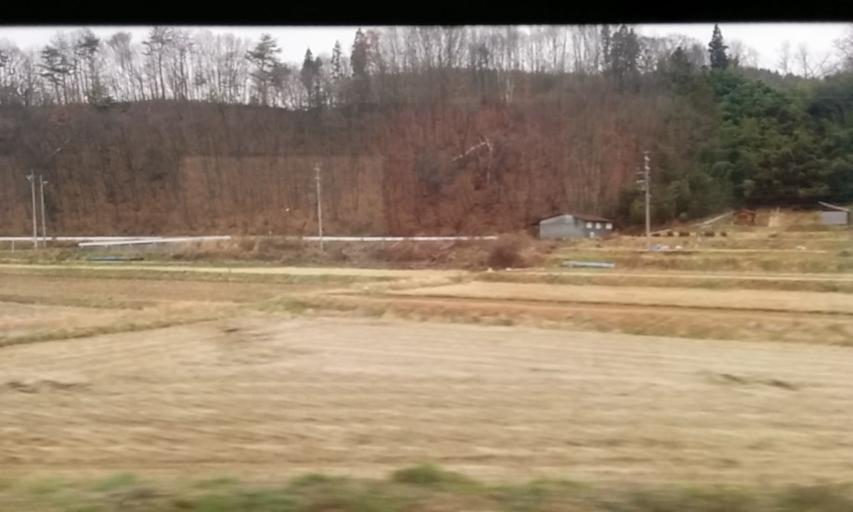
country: JP
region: Nagano
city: Omachi
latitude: 36.4427
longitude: 138.0230
